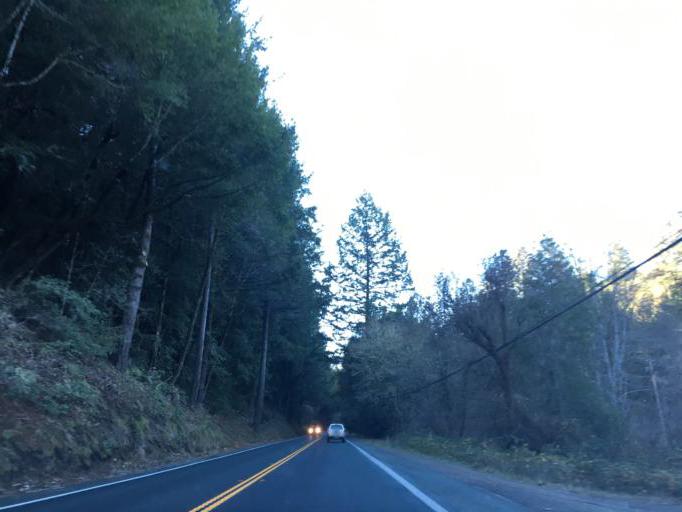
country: US
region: California
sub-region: Mendocino County
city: Brooktrails
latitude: 39.5077
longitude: -123.3824
